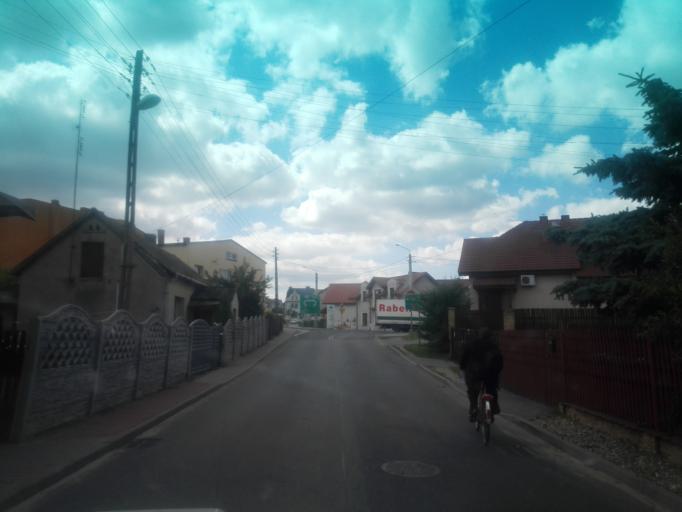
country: PL
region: Silesian Voivodeship
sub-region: Powiat czestochowski
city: Olsztyn
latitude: 50.7512
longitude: 19.2678
